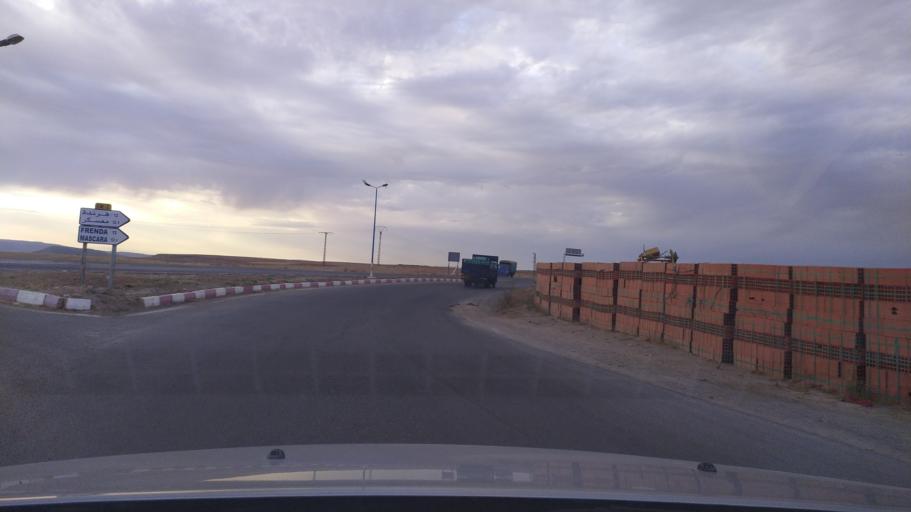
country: DZ
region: Tiaret
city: Frenda
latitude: 34.9923
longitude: 1.1301
